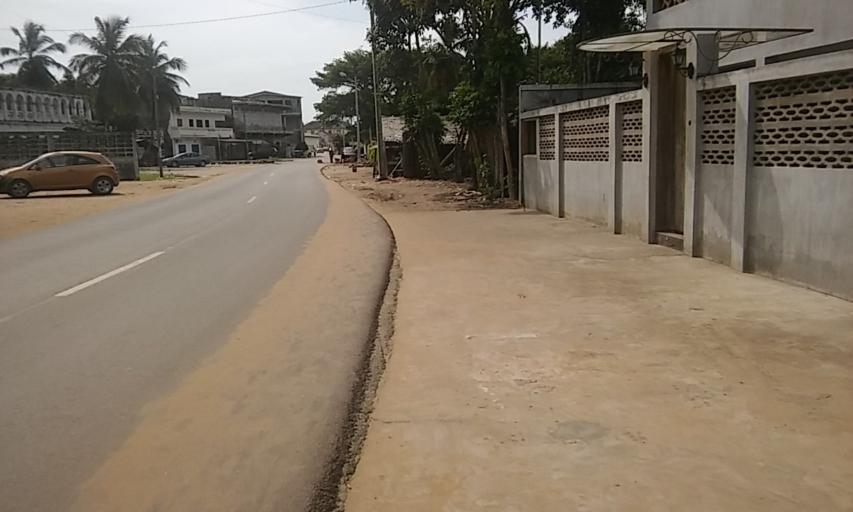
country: CI
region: Sud-Comoe
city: Grand-Bassam
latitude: 5.1962
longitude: -3.7297
